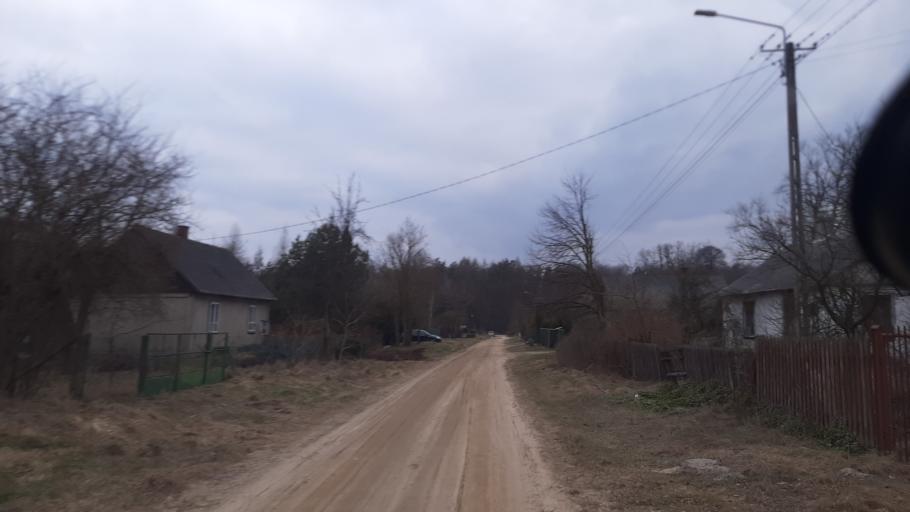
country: PL
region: Lublin Voivodeship
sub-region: Powiat lubelski
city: Garbow
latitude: 51.3998
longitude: 22.3911
